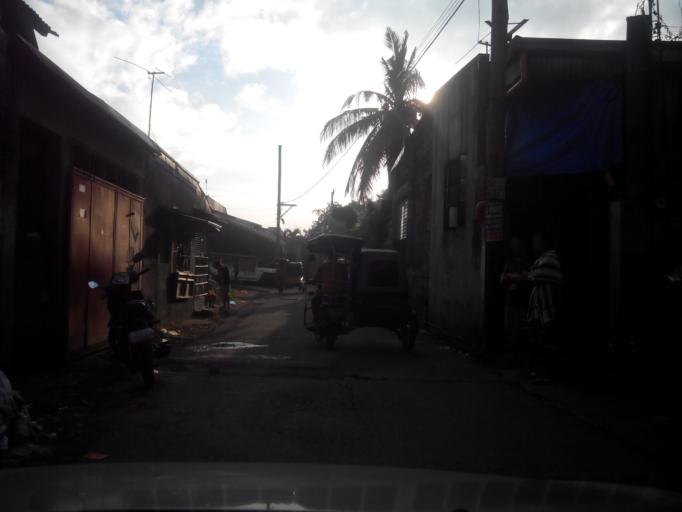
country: PH
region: Calabarzon
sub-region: Province of Rizal
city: Taytay
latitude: 14.5647
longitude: 121.1281
